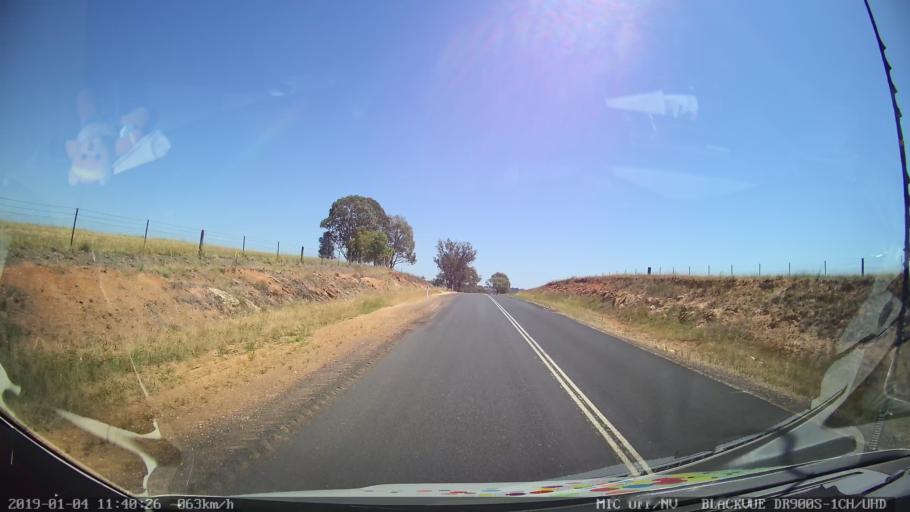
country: AU
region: New South Wales
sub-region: Cabonne
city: Molong
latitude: -33.0049
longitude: 148.7871
